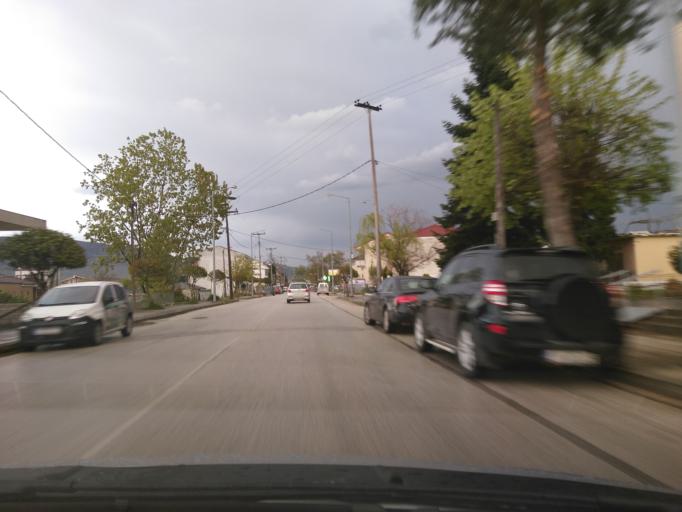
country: GR
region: Epirus
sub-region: Nomos Ioanninon
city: Katsikas
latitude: 39.6255
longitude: 20.8849
